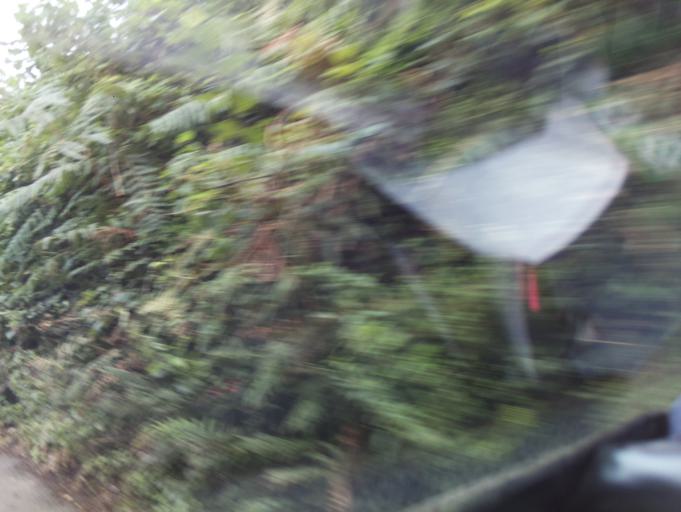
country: GB
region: England
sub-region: Devon
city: Dartmouth
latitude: 50.3433
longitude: -3.6252
